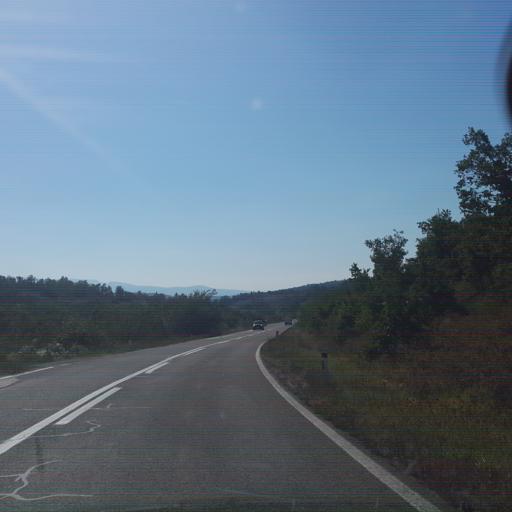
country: RS
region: Central Serbia
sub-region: Zajecarski Okrug
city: Knjazevac
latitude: 43.4697
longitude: 22.2218
